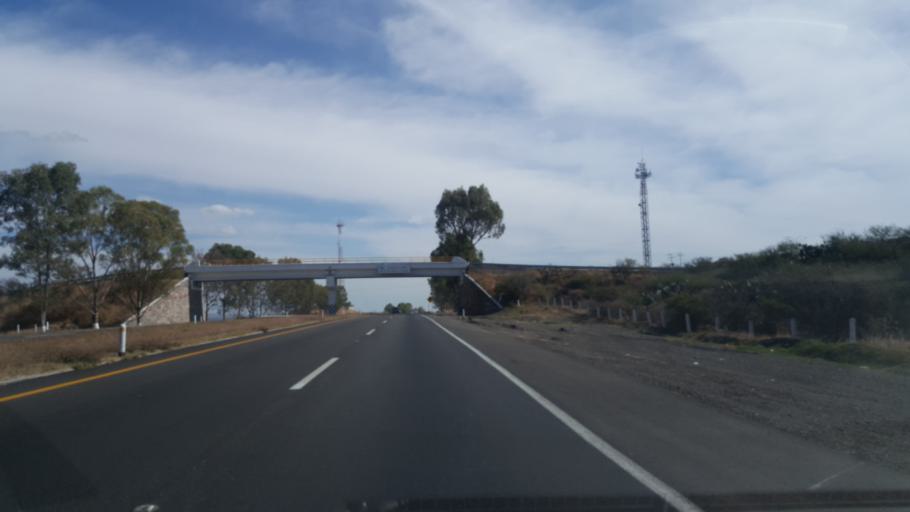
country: MX
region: Jalisco
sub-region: Lagos de Moreno
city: Cristeros [Fraccionamiento]
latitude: 21.2651
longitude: -101.9631
